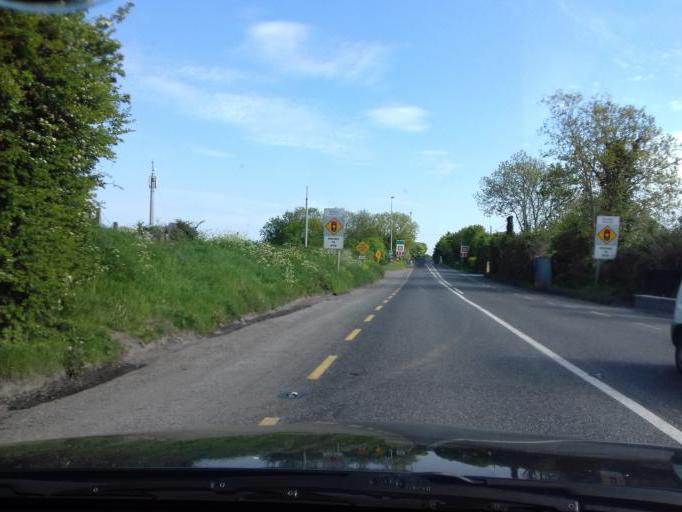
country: IE
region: Leinster
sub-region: Dublin City
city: Finglas
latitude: 53.4262
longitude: -6.3283
